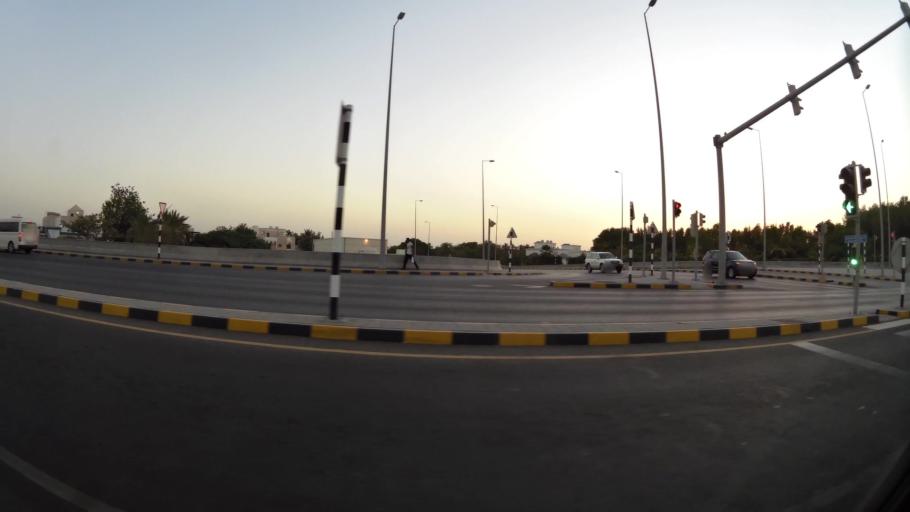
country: OM
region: Muhafazat Masqat
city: As Sib al Jadidah
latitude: 23.6709
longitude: 58.1908
